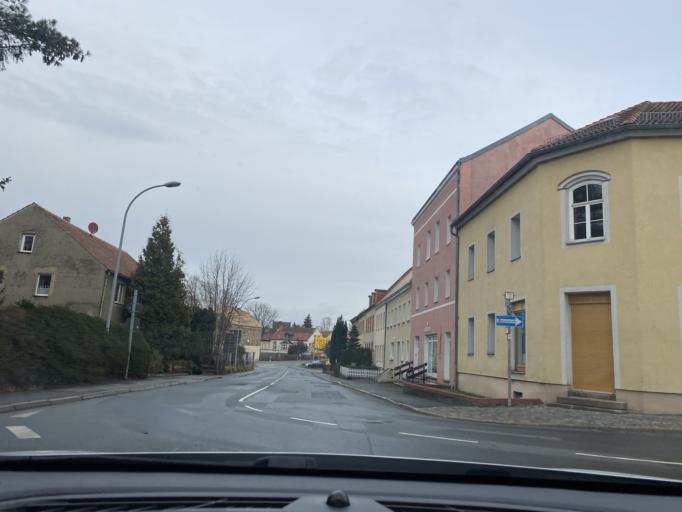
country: DE
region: Saxony
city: Reichenbach
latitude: 51.1398
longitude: 14.7976
